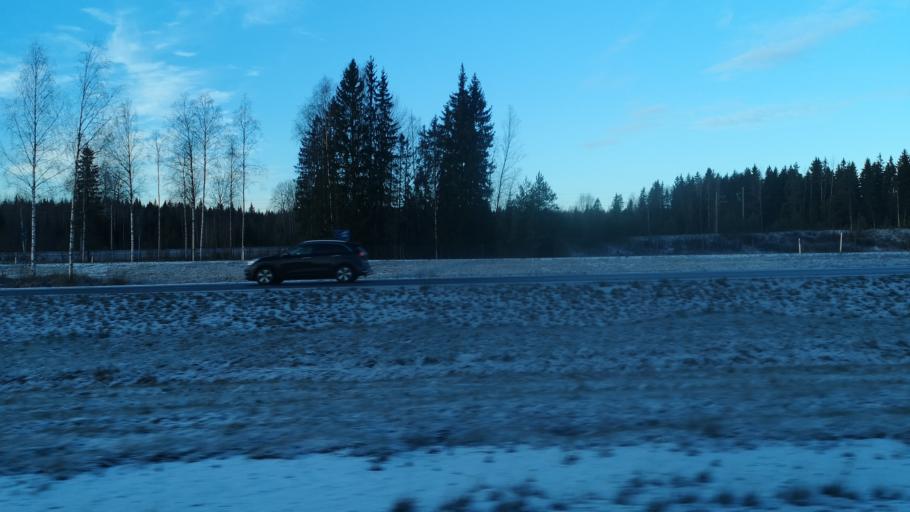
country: FI
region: Uusimaa
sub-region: Helsinki
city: Jaervenpaeae
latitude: 60.5502
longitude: 25.1847
